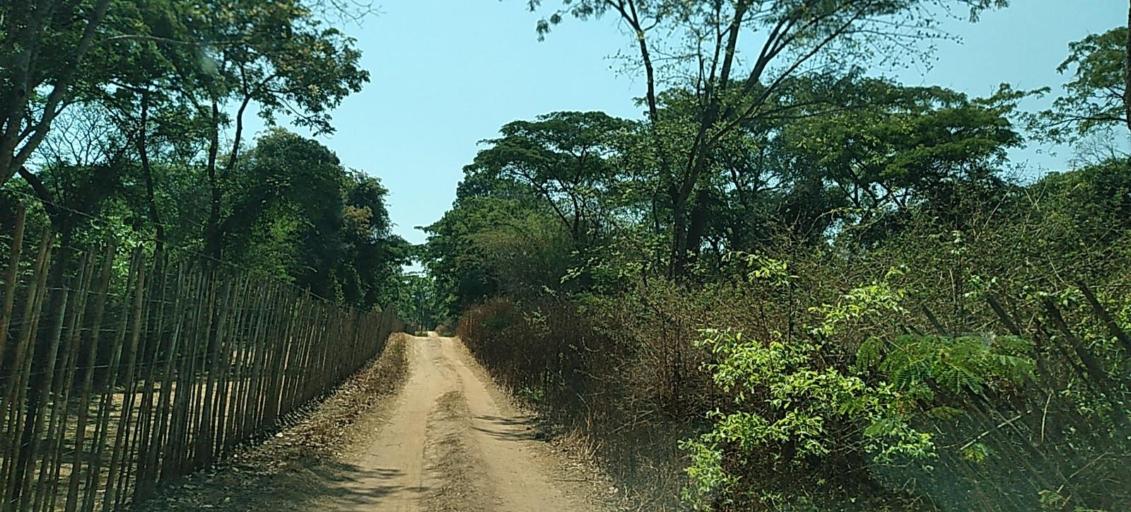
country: ZM
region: Copperbelt
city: Luanshya
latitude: -13.0091
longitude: 28.4605
